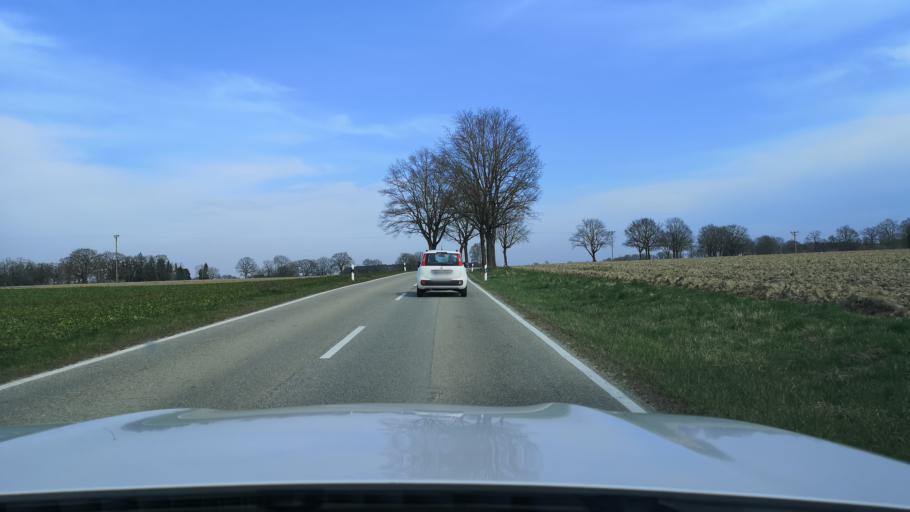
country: DE
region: Bavaria
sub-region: Upper Bavaria
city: Ottenhofen
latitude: 48.1967
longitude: 11.9011
